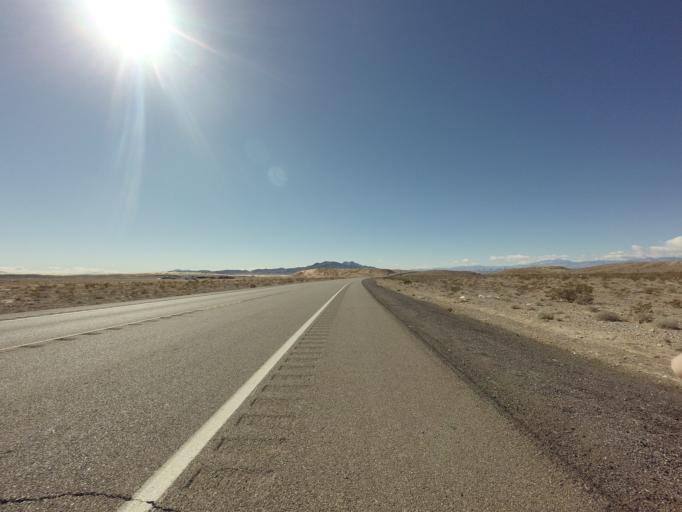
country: US
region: Nevada
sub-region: Clark County
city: Nellis Air Force Base
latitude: 36.3068
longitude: -114.9534
